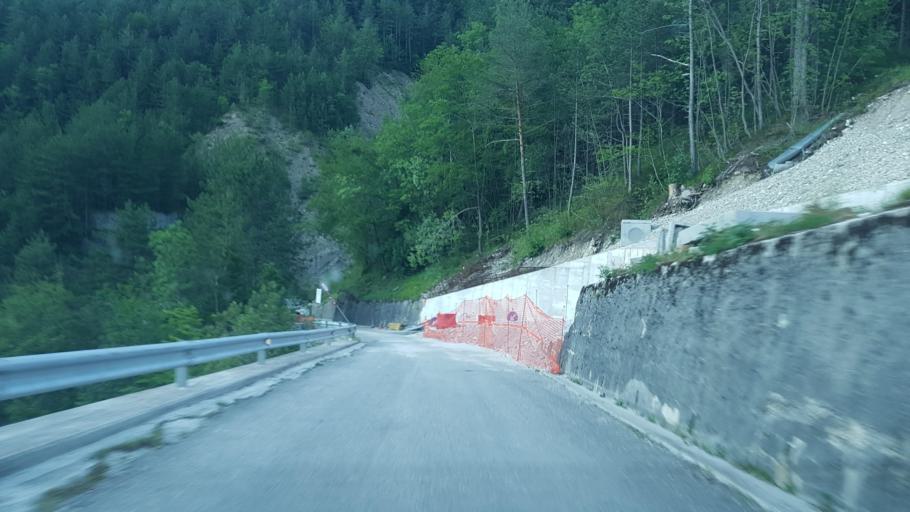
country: IT
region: Friuli Venezia Giulia
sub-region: Provincia di Udine
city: Dogna
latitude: 46.4489
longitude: 13.3567
